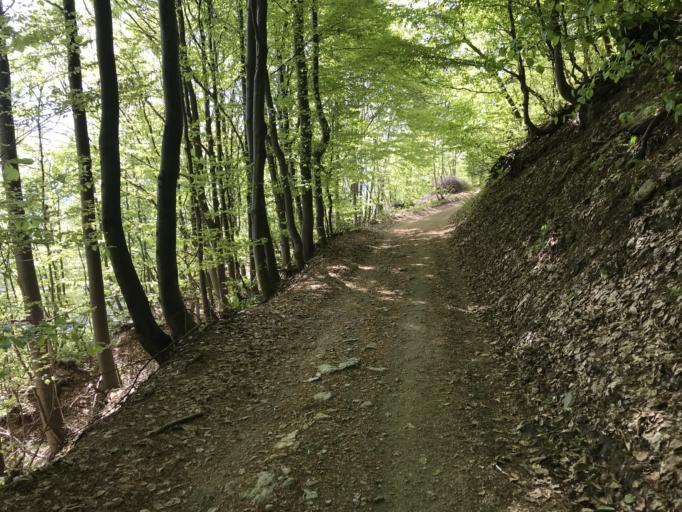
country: IT
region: Piedmont
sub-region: Provincia di Cuneo
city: Robilante
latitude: 44.2924
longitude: 7.5499
